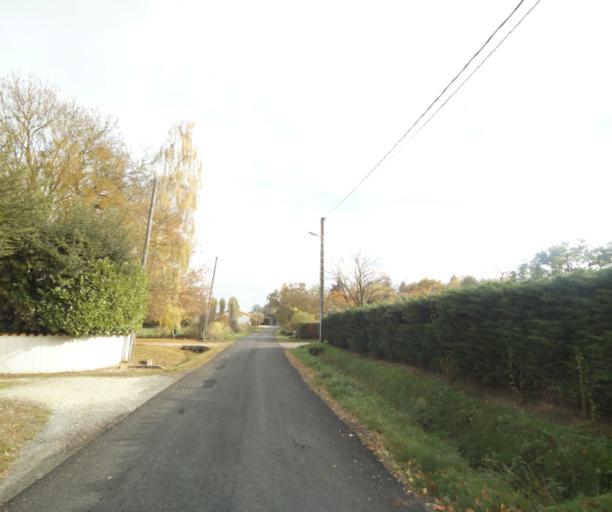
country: FR
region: Poitou-Charentes
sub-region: Departement de la Charente-Maritime
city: Saint-Georges-des-Coteaux
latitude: 45.7622
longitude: -0.7001
